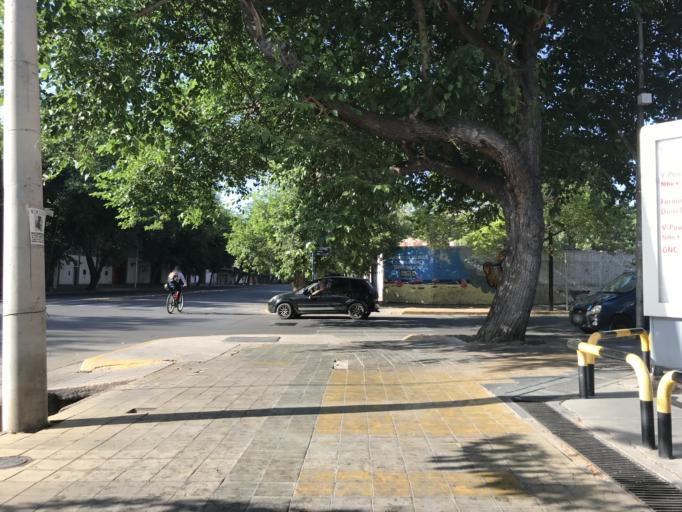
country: AR
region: Mendoza
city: Mendoza
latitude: -32.8815
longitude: -68.8425
